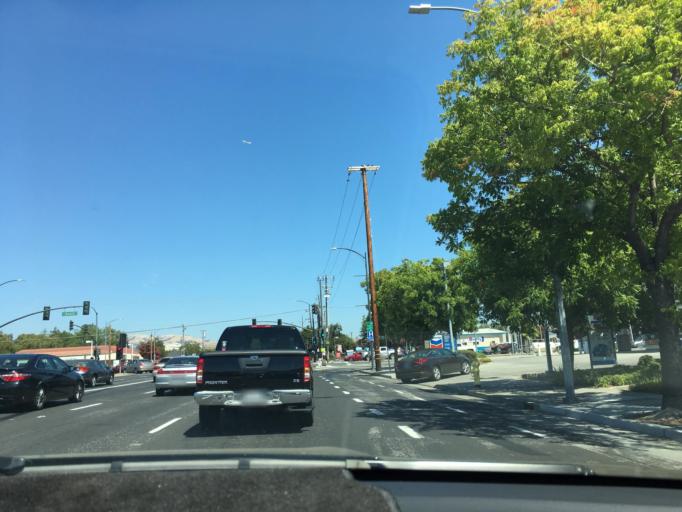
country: US
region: California
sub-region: Santa Clara County
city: Seven Trees
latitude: 37.2512
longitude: -121.8318
